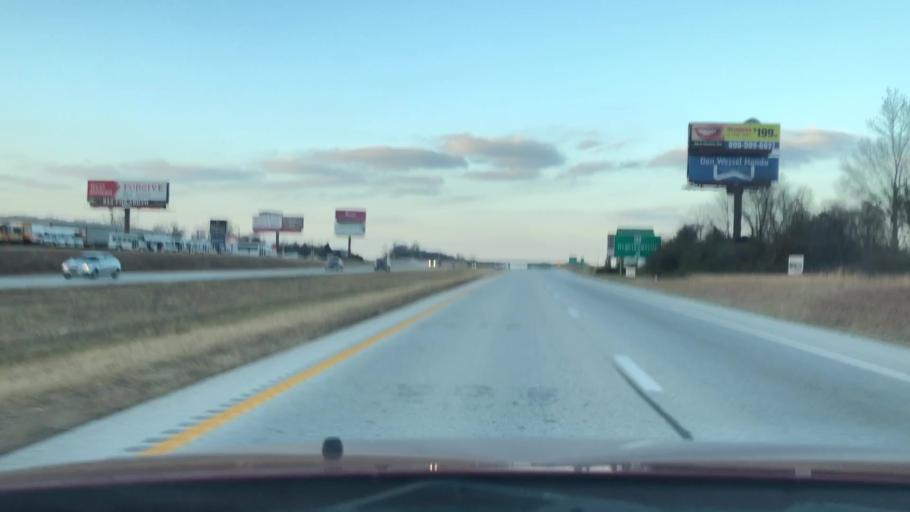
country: US
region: Missouri
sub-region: Christian County
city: Ozark
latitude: 36.9371
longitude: -93.2320
